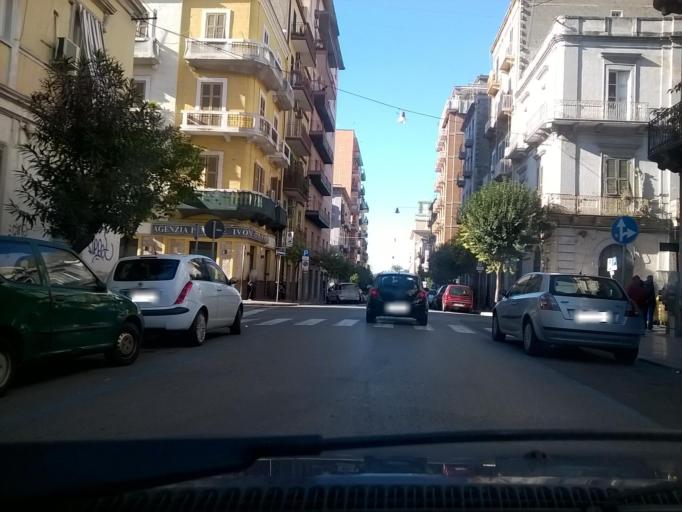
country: IT
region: Apulia
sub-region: Provincia di Taranto
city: Taranto
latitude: 40.4662
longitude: 17.2464
